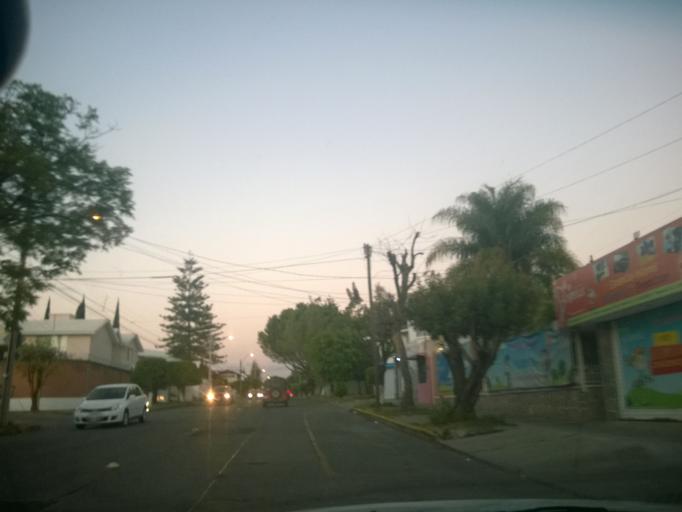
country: MX
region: Guanajuato
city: Leon
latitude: 21.1468
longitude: -101.6949
